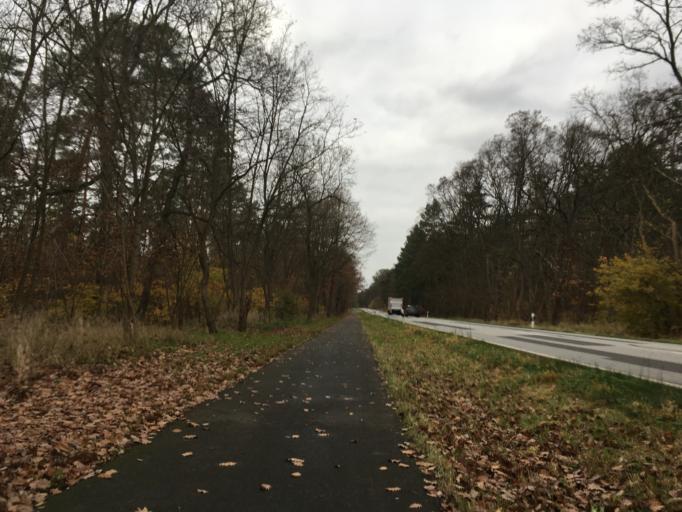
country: DE
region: Brandenburg
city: Mullrose
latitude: 52.2115
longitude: 14.4517
